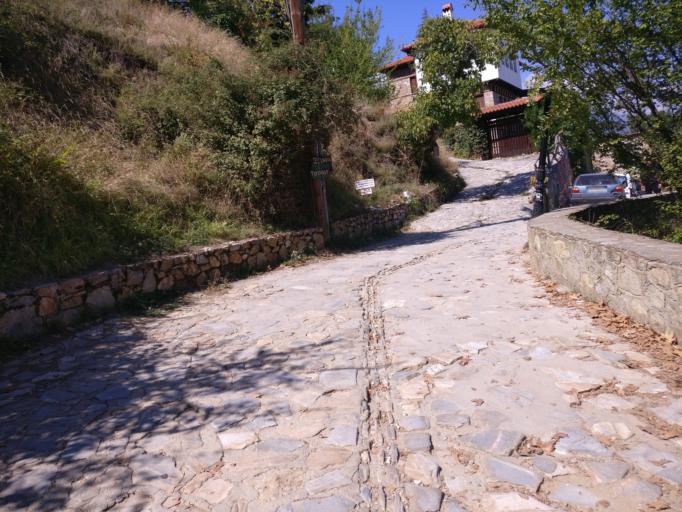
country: GR
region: Central Macedonia
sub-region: Nomos Pierias
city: Leptokarya
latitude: 39.9907
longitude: 22.5718
